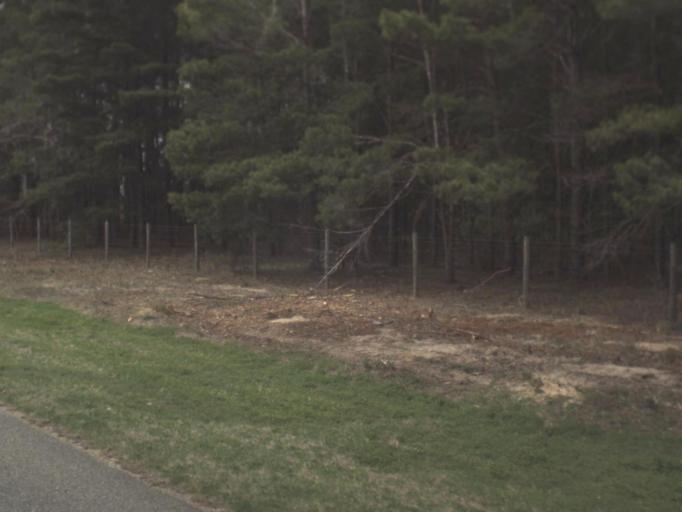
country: US
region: Florida
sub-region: Liberty County
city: Bristol
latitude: 30.4732
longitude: -84.9329
